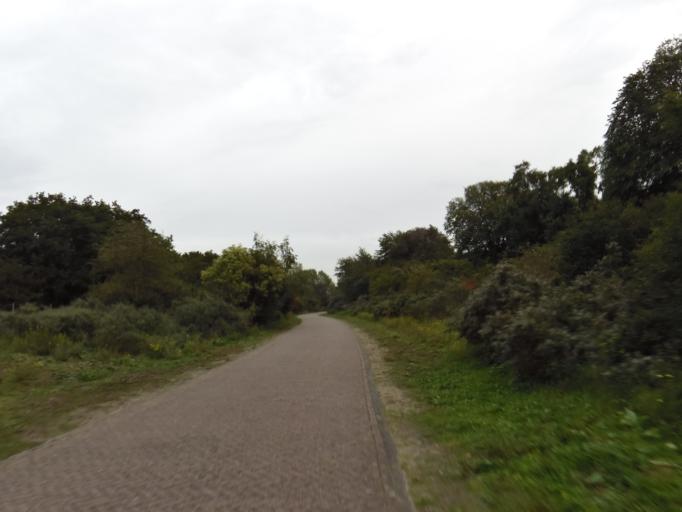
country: NL
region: South Holland
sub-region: Gemeente Den Haag
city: Scheveningen
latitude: 52.1102
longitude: 4.3056
